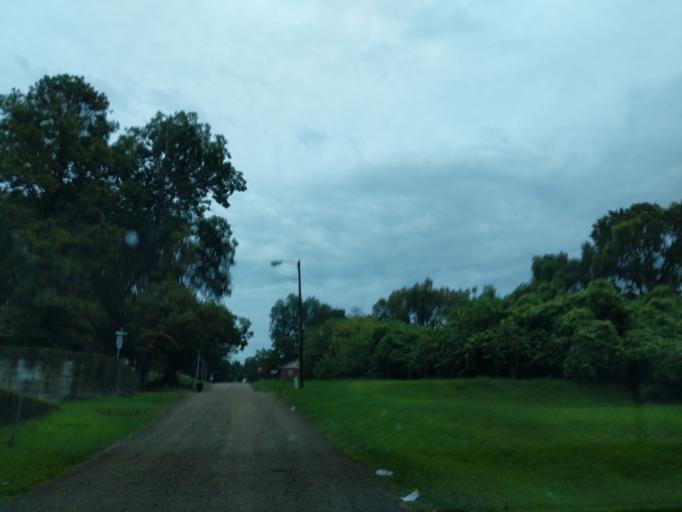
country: US
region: Mississippi
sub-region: Warren County
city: Vicksburg
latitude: 32.3346
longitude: -90.8903
